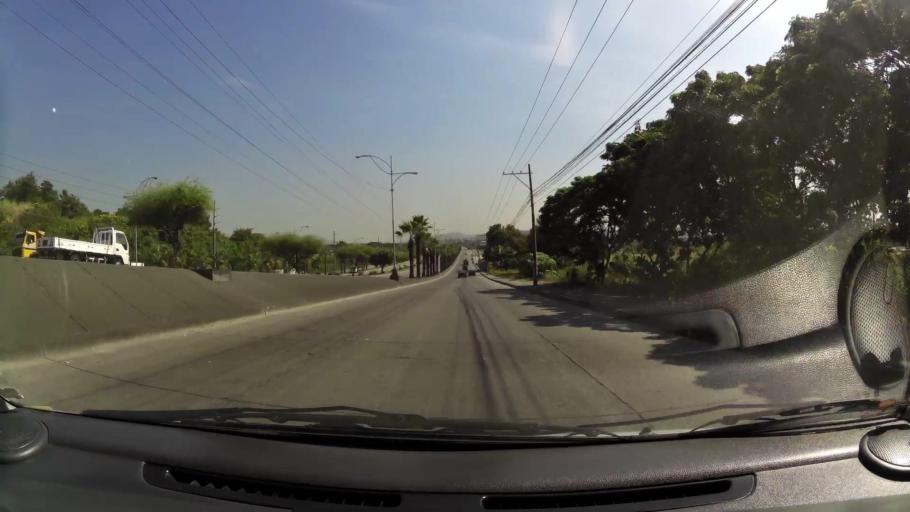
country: EC
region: Guayas
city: Eloy Alfaro
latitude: -2.1074
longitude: -79.9087
